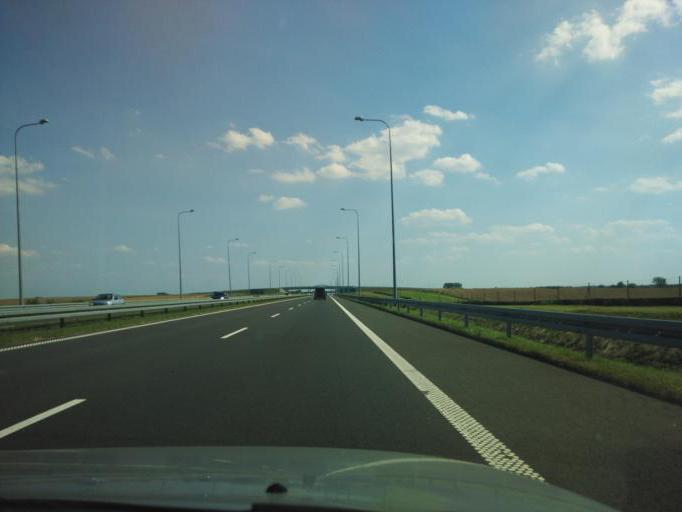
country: PL
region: West Pomeranian Voivodeship
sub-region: Powiat pyrzycki
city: Bielice
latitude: 53.1297
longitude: 14.7303
